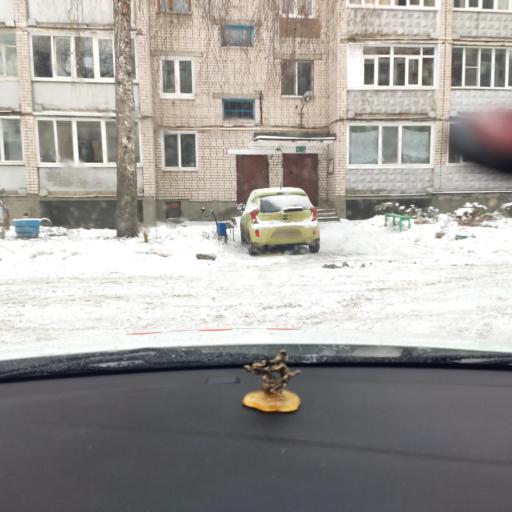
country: RU
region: Tatarstan
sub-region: Zelenodol'skiy Rayon
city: Zelenodolsk
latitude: 55.8505
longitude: 48.5587
